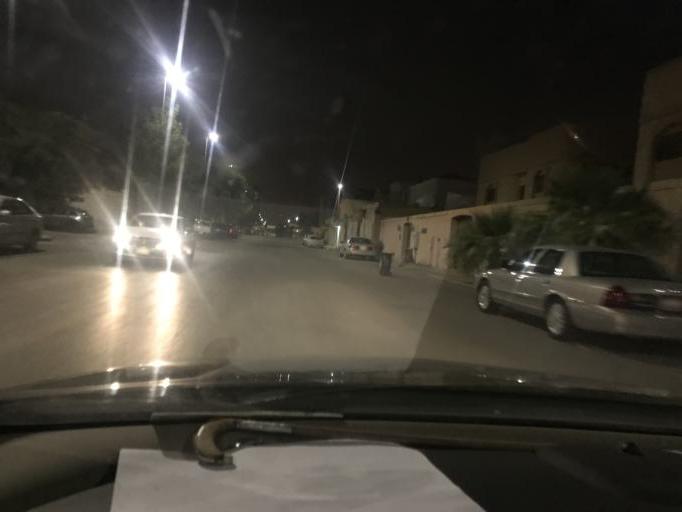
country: SA
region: Ar Riyad
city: Riyadh
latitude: 24.7246
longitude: 46.7733
